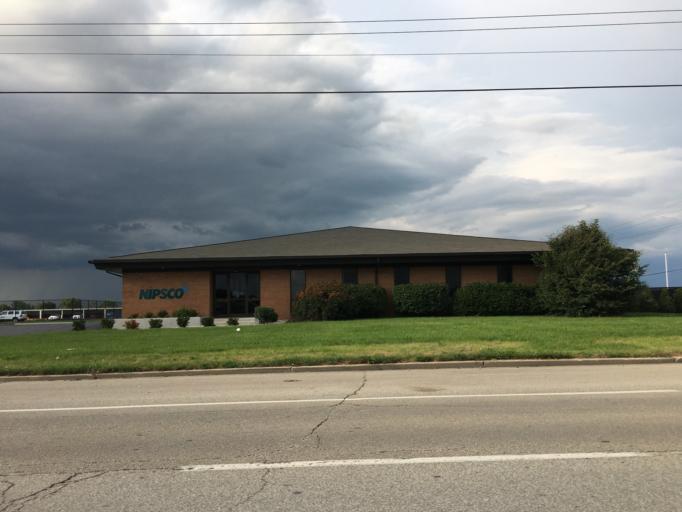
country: US
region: Indiana
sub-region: Howard County
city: Kokomo
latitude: 40.4625
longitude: -86.1194
